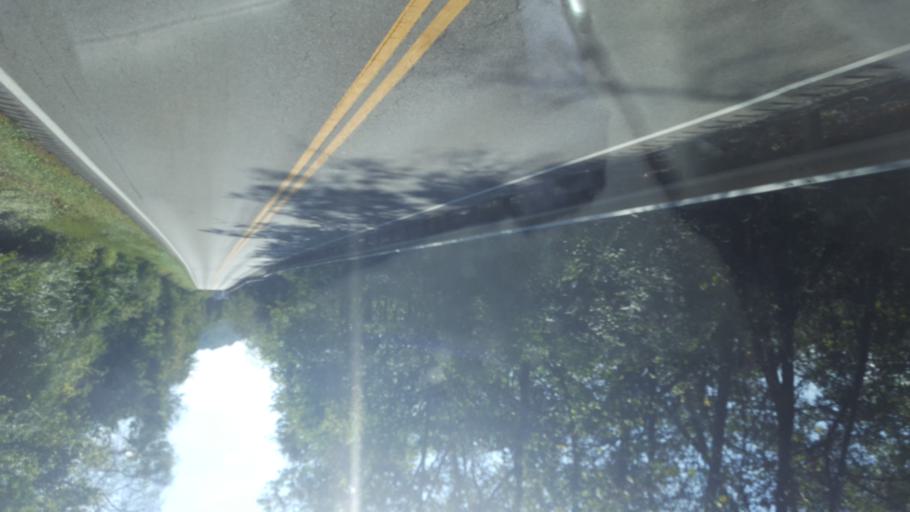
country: US
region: Ohio
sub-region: Brown County
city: Aberdeen
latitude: 38.6651
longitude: -83.7803
